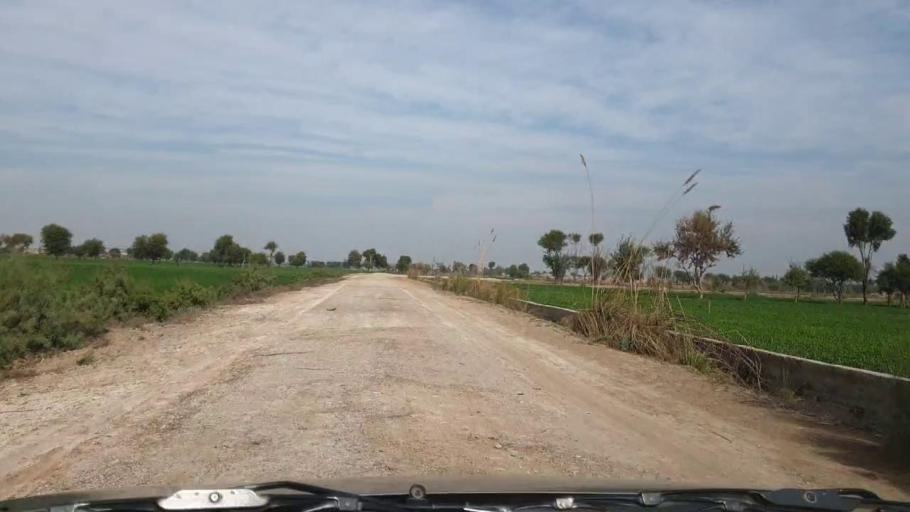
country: PK
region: Sindh
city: Jam Sahib
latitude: 26.2907
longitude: 68.6927
